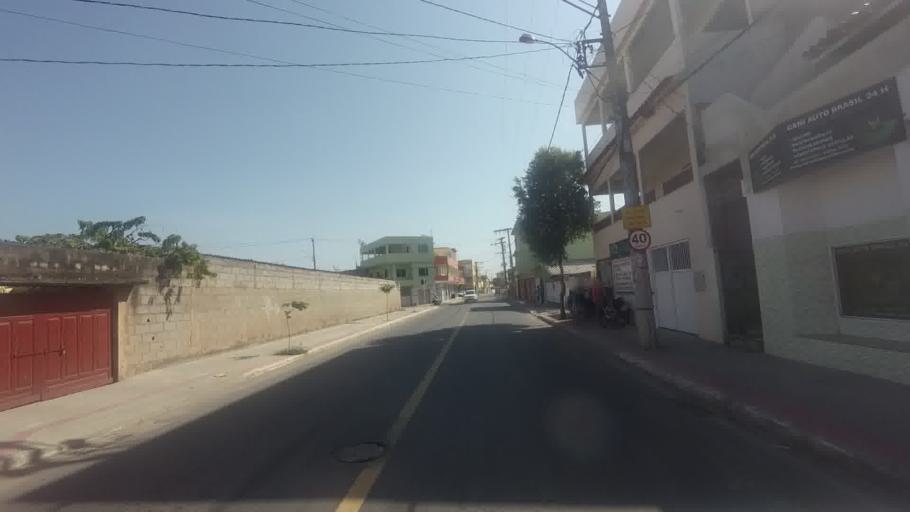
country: BR
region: Espirito Santo
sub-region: Piuma
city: Piuma
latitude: -20.8391
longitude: -40.7303
